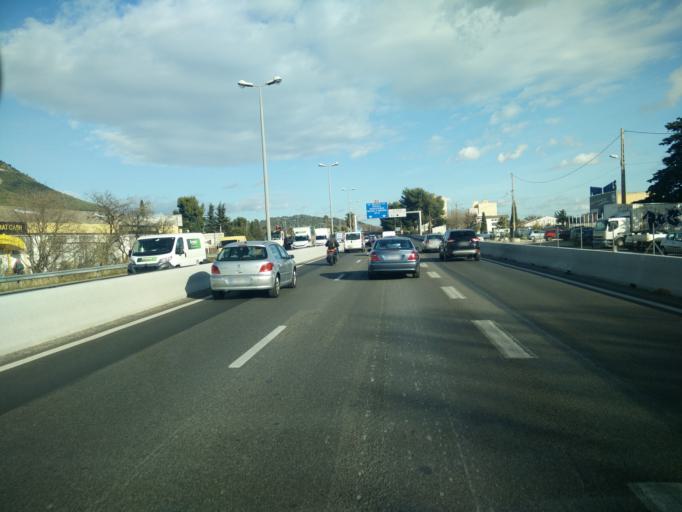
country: FR
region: Provence-Alpes-Cote d'Azur
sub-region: Departement du Var
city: La Valette-du-Var
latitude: 43.1356
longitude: 5.9905
